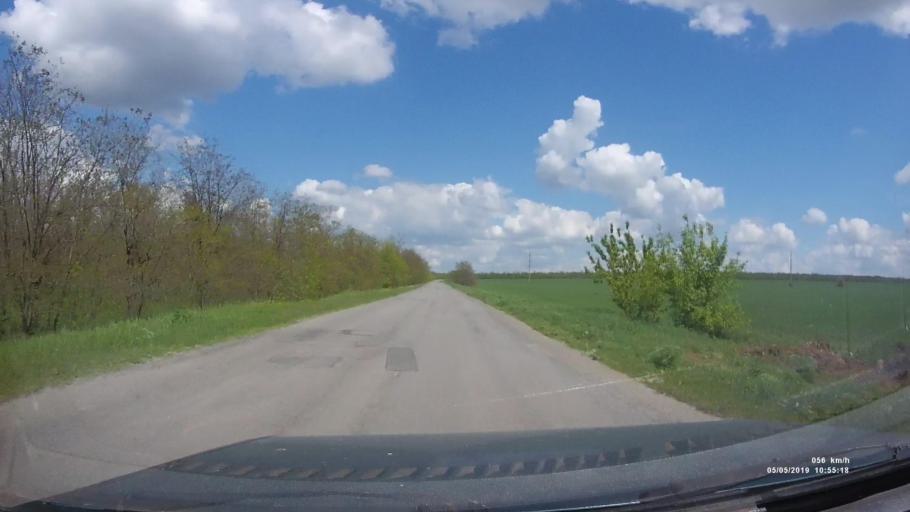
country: RU
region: Rostov
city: Ust'-Donetskiy
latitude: 47.6645
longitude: 40.8214
